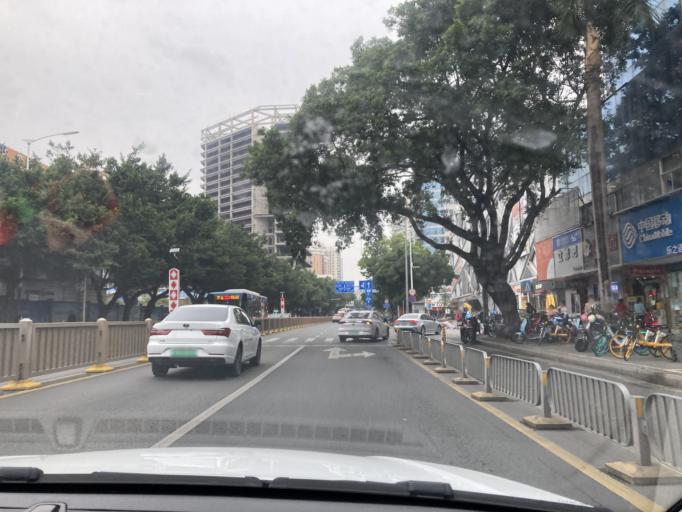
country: CN
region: Guangdong
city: Nantou
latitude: 22.5372
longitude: 113.9145
